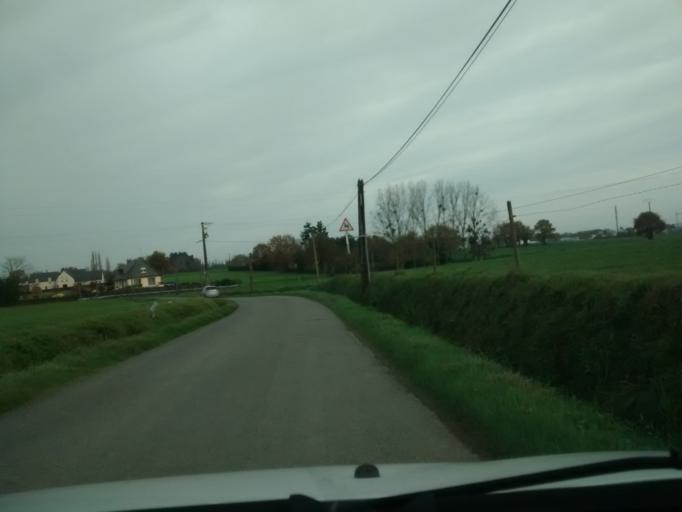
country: FR
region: Brittany
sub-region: Departement d'Ille-et-Vilaine
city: Noyal-sur-Vilaine
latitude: 48.0986
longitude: -1.5315
